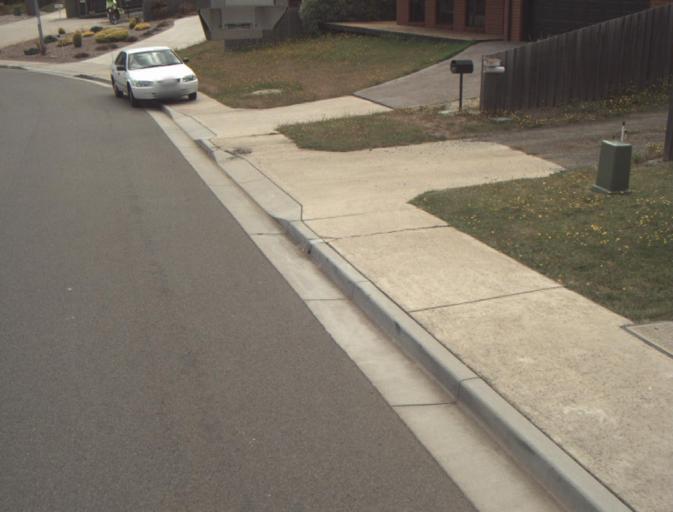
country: AU
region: Tasmania
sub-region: Launceston
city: West Launceston
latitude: -41.4570
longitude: 147.1228
